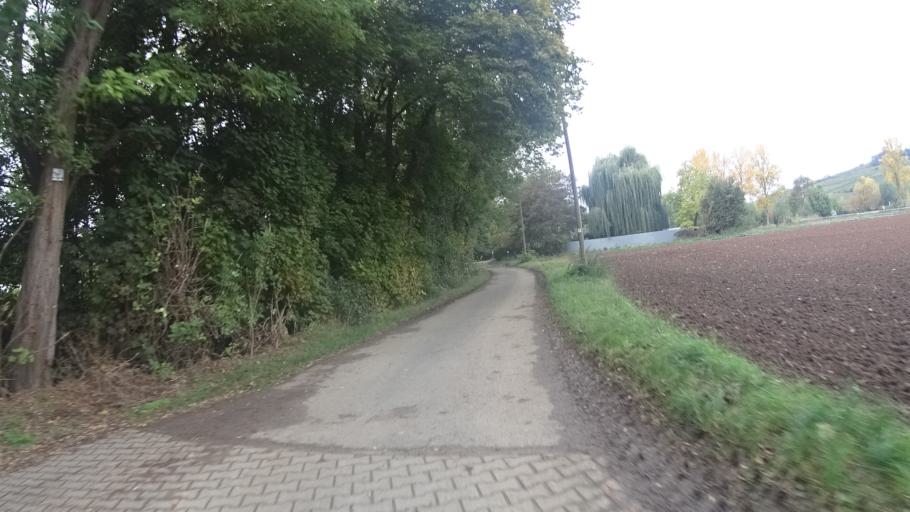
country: DE
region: Rheinland-Pfalz
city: Molsheim
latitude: 49.6387
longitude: 8.1718
